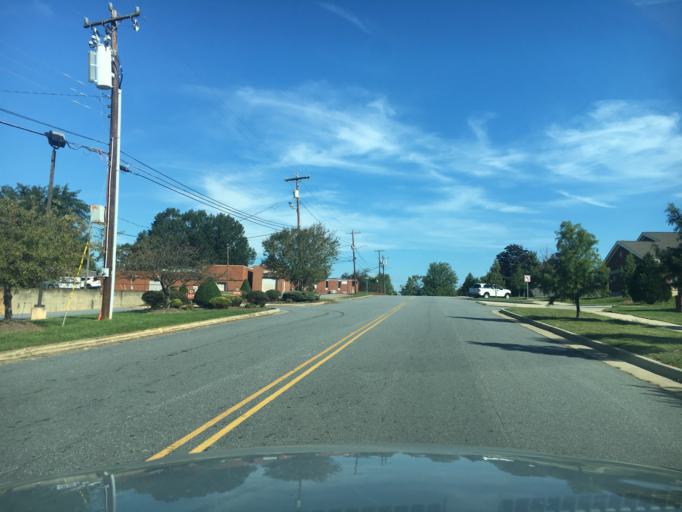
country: US
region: North Carolina
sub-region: Catawba County
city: Hickory
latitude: 35.7227
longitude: -81.3613
